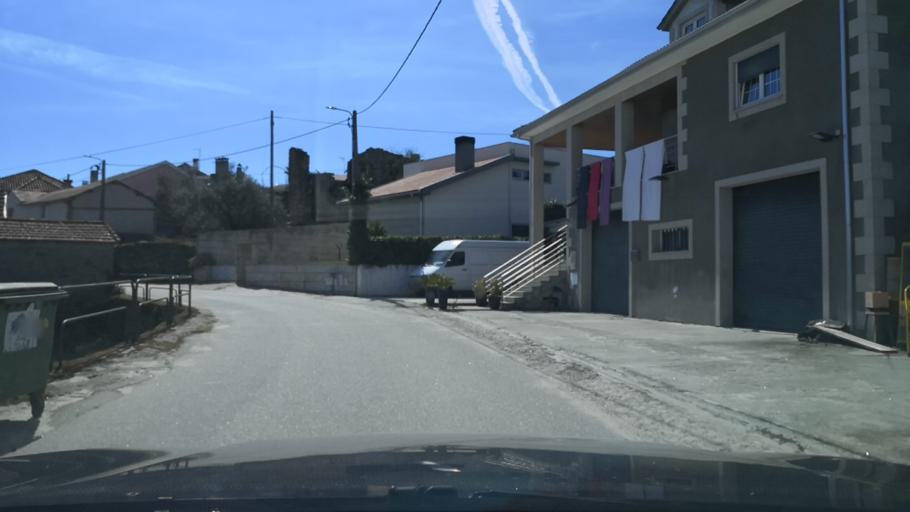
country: PT
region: Vila Real
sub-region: Sabrosa
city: Sabrosa
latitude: 41.3372
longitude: -7.5898
